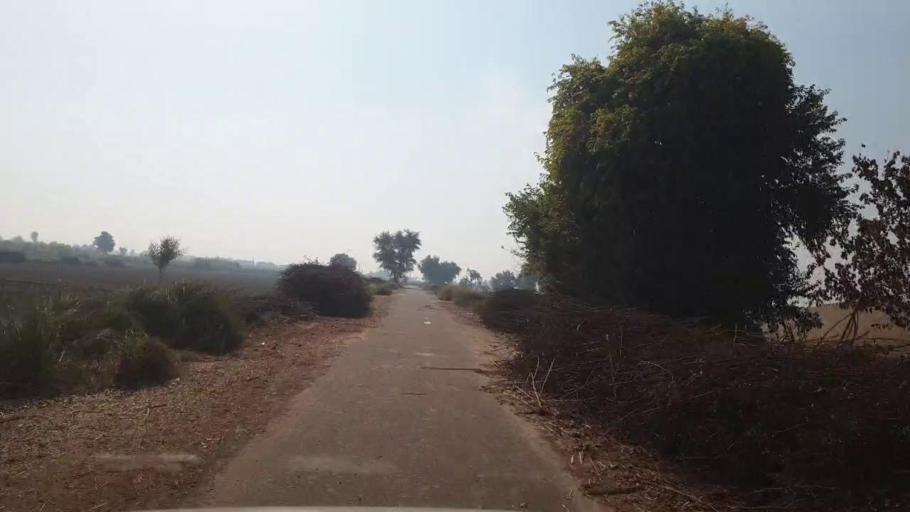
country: PK
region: Sindh
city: Bhan
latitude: 26.6108
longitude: 67.7603
